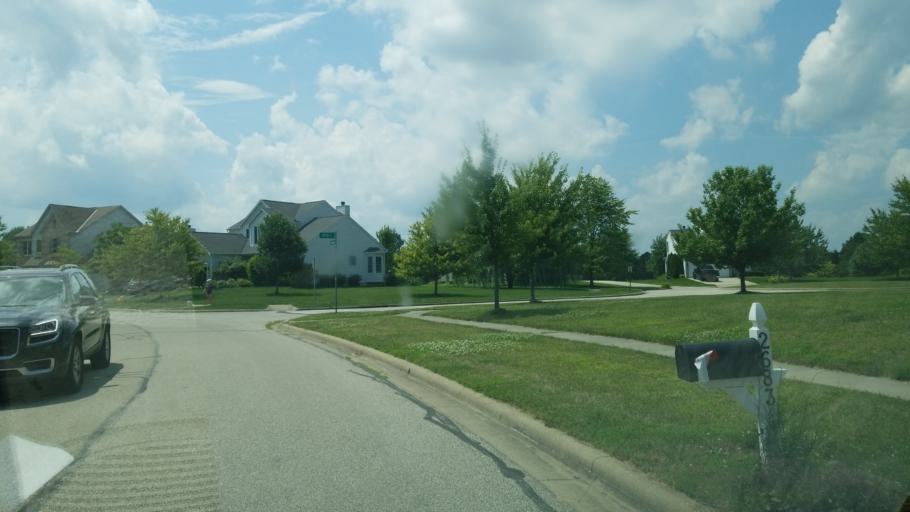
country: US
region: Ohio
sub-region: Delaware County
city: Lewis Center
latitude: 40.2184
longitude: -82.9977
